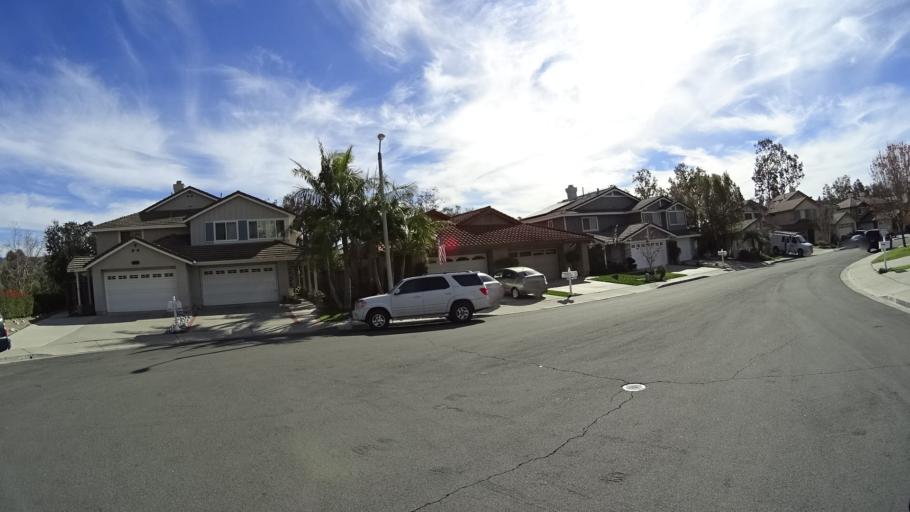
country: US
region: California
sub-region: Orange County
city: Portola Hills
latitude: 33.6838
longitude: -117.6261
